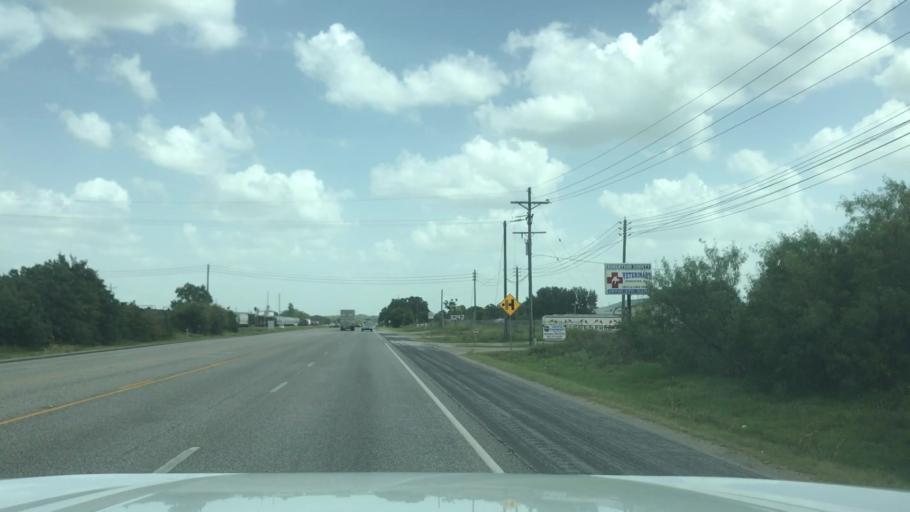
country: US
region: Texas
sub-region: Robertson County
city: Hearne
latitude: 30.8580
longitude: -96.5759
